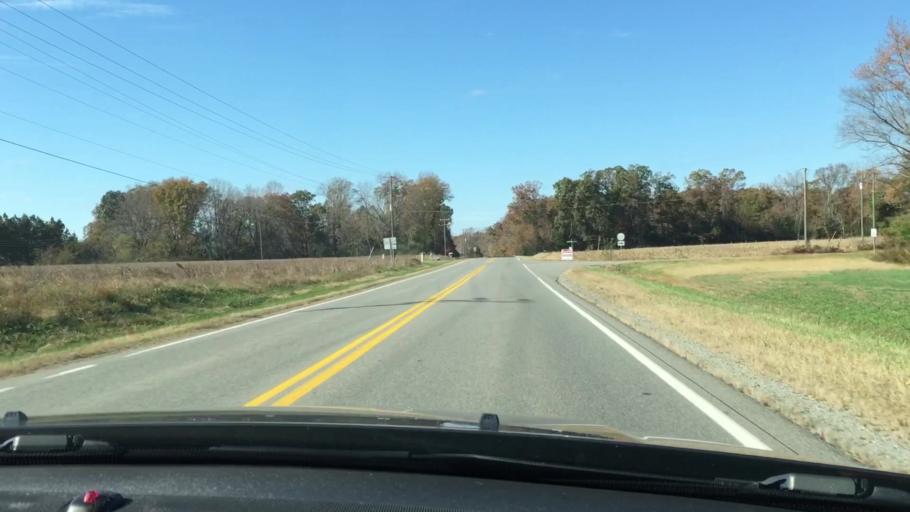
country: US
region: Virginia
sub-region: King William County
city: King William
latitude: 37.7097
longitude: -77.0562
